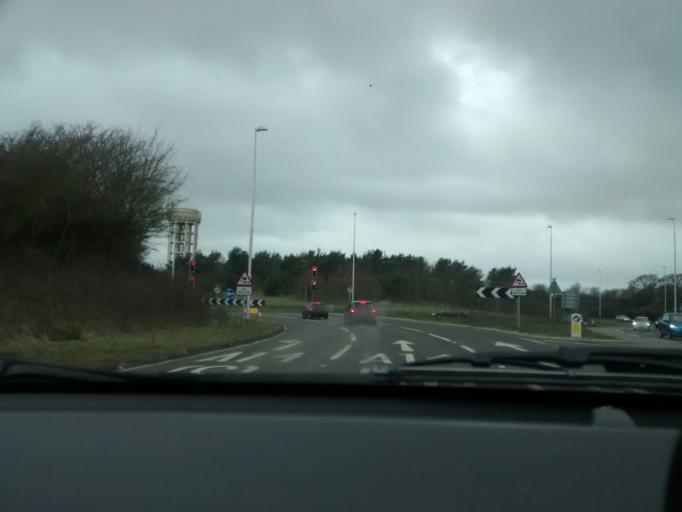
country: GB
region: England
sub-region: Suffolk
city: Felixstowe
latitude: 51.9782
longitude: 1.3339
